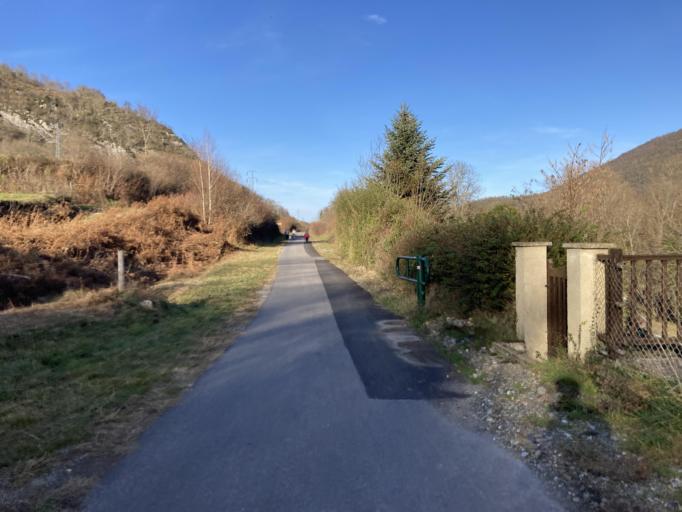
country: FR
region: Aquitaine
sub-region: Departement des Pyrenees-Atlantiques
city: Louvie-Juzon
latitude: 43.0649
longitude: -0.4246
